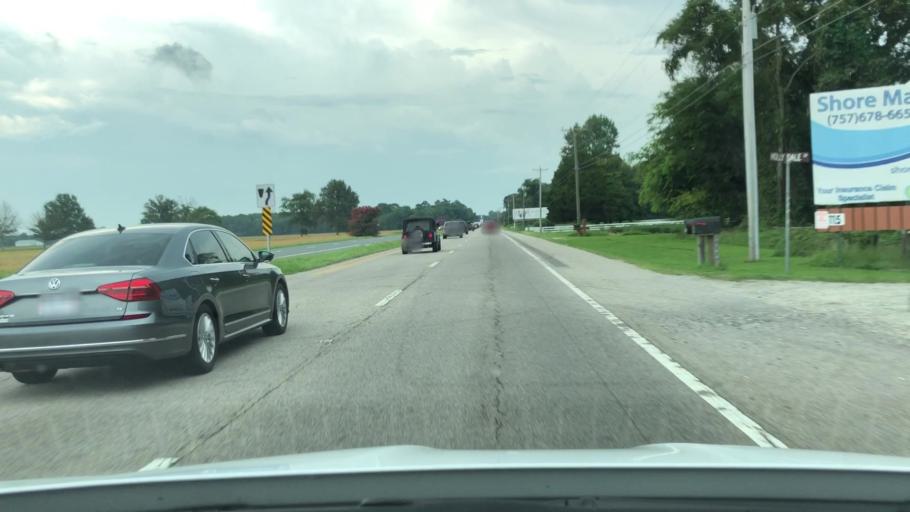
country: US
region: Virginia
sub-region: Northampton County
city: Cape Charles
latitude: 37.2421
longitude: -75.9716
